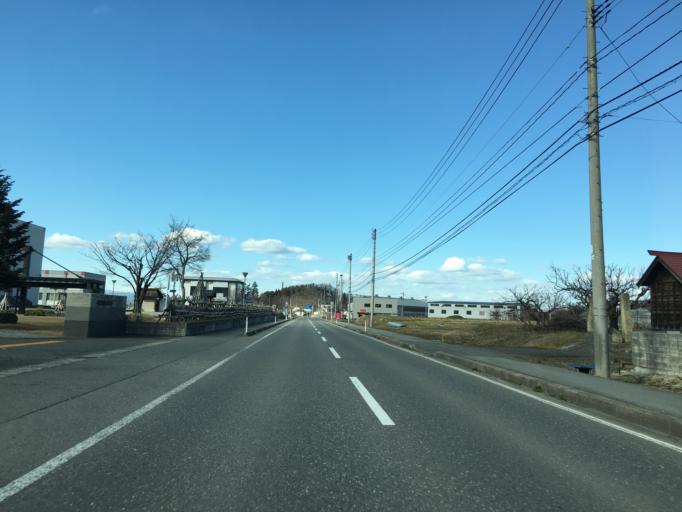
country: JP
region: Yamagata
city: Yonezawa
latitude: 37.9165
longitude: 140.1460
